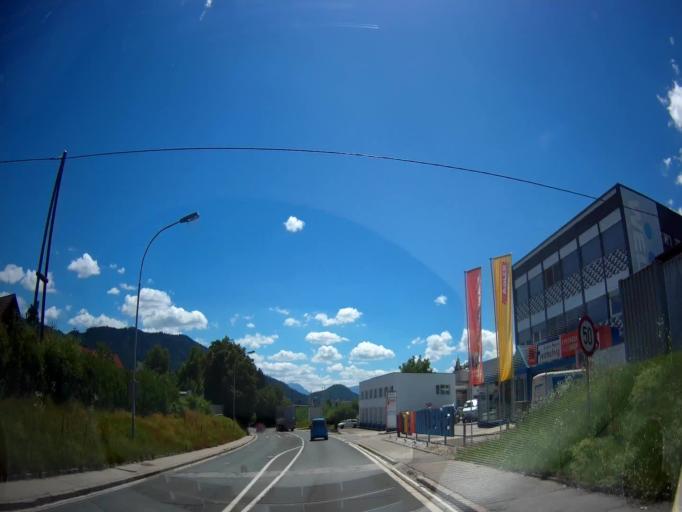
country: AT
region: Carinthia
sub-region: Politischer Bezirk Sankt Veit an der Glan
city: Sankt Veit an der Glan
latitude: 46.7510
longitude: 14.3802
